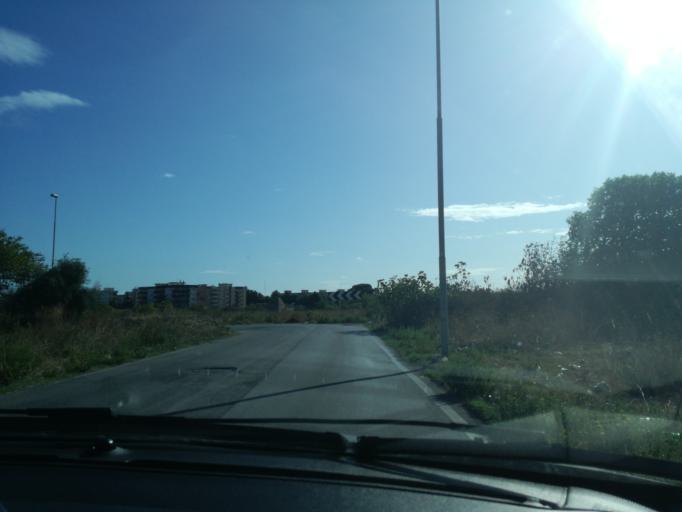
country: IT
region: Apulia
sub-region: Provincia di Bari
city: Triggiano
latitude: 41.0696
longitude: 16.9235
